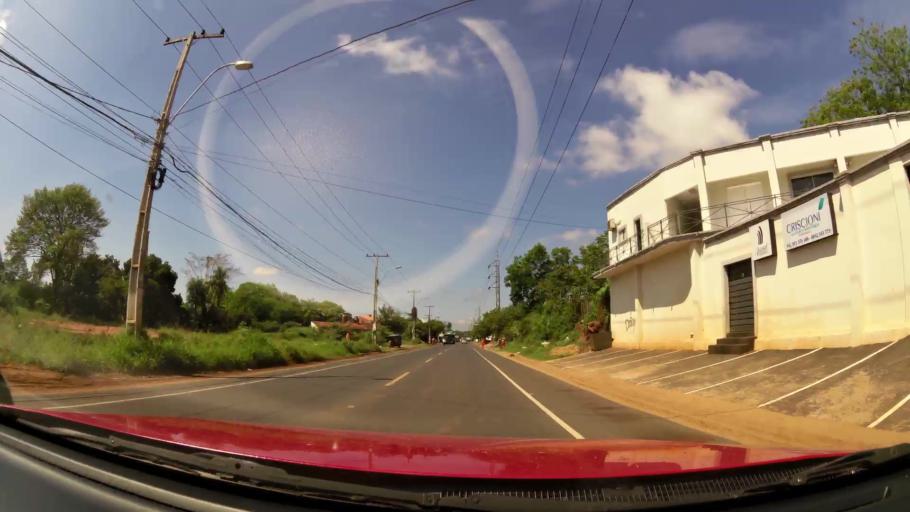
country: PY
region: Central
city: San Lorenzo
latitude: -25.3278
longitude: -57.5095
